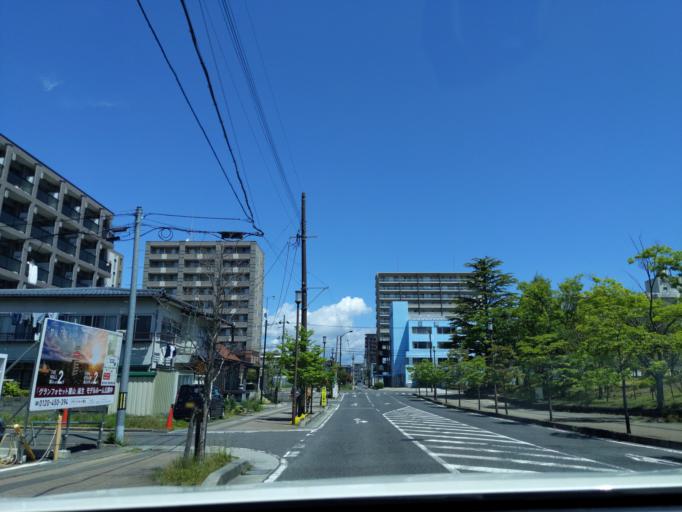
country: JP
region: Fukushima
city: Koriyama
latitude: 37.3960
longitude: 140.3733
